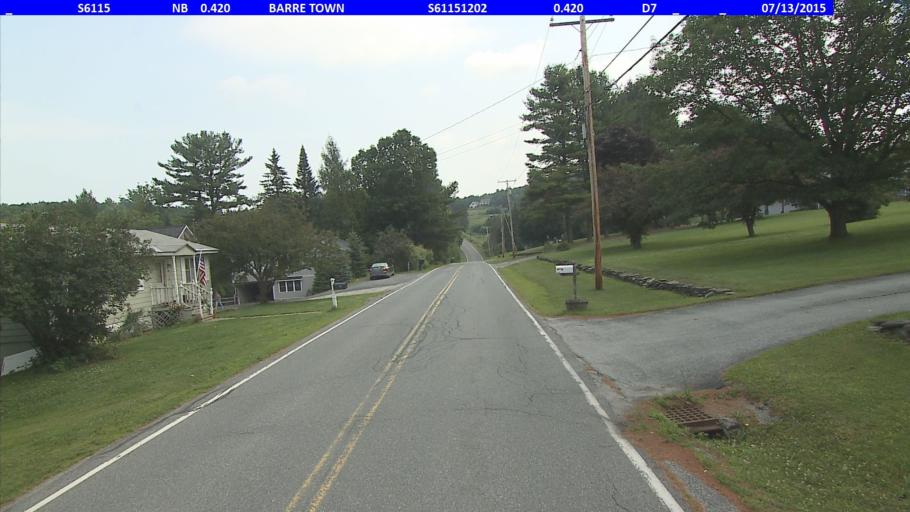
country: US
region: Vermont
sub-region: Washington County
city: Barre
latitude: 44.2054
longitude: -72.4825
